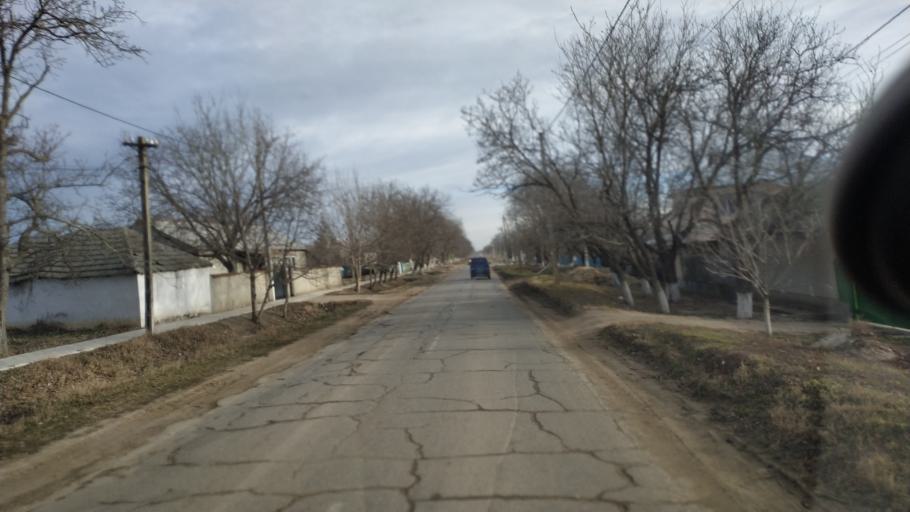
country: MD
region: Criuleni
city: Criuleni
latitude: 47.1679
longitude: 29.1245
